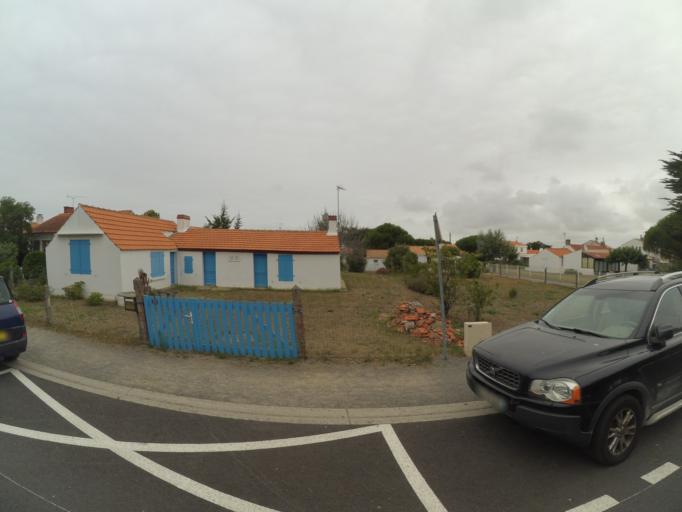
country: FR
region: Pays de la Loire
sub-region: Departement de la Vendee
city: La Barre-de-Monts
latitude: 46.8903
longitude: -2.1276
